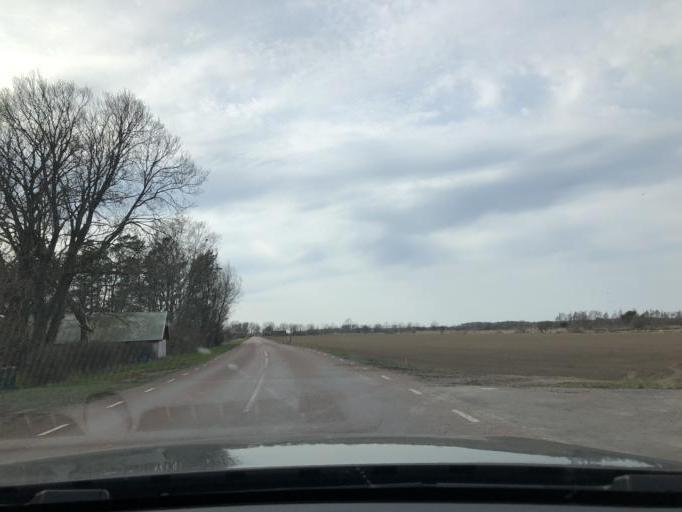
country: SE
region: Kalmar
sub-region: Morbylanga Kommun
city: Moerbylanga
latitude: 56.2866
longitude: 16.4897
